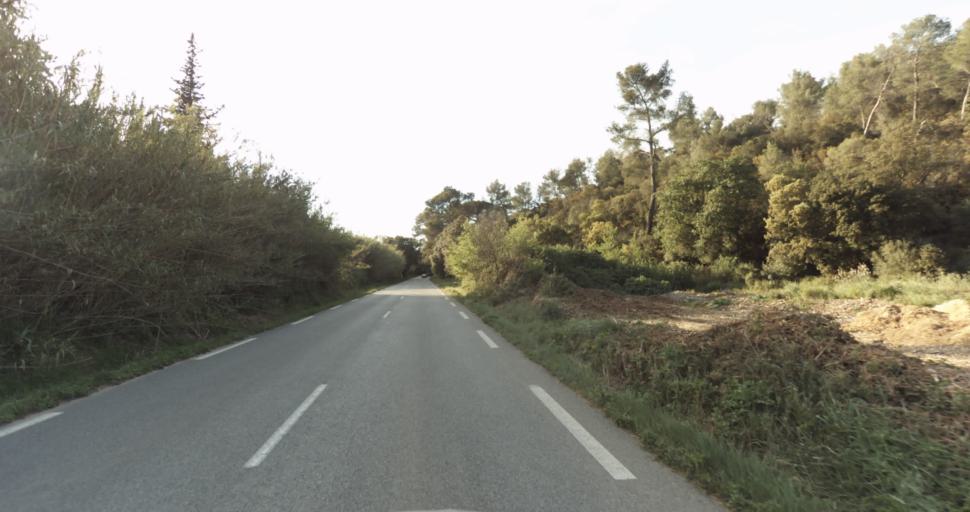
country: FR
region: Provence-Alpes-Cote d'Azur
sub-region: Departement du Var
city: Hyeres
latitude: 43.1629
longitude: 6.1224
